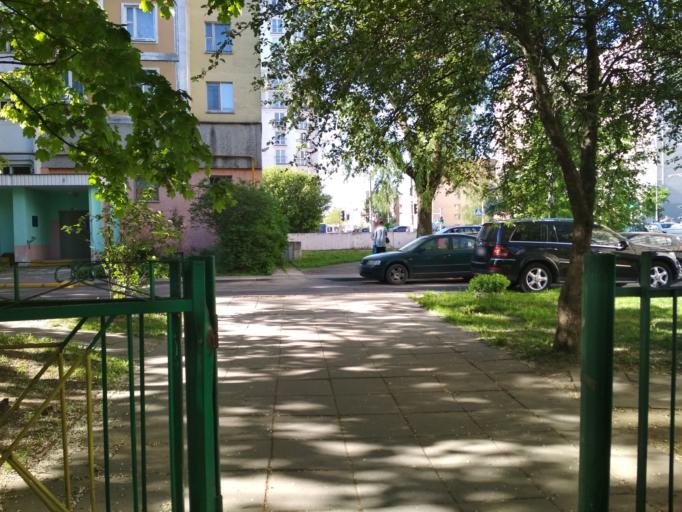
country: BY
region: Minsk
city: Minsk
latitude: 53.8786
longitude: 27.5437
